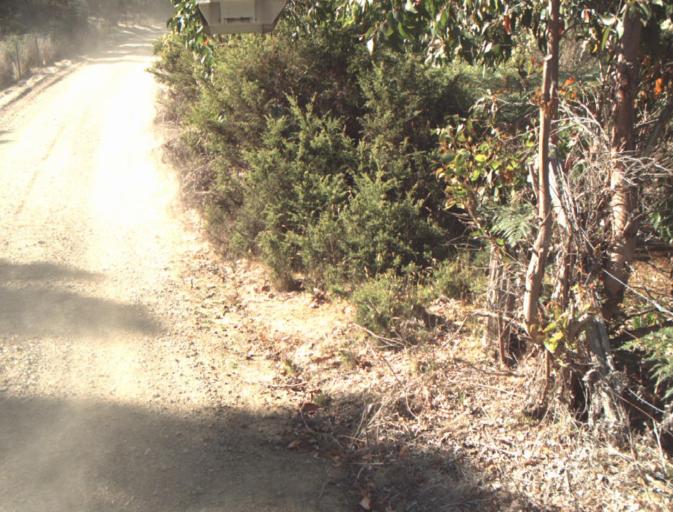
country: AU
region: Tasmania
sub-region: Dorset
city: Scottsdale
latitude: -41.3022
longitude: 147.3581
